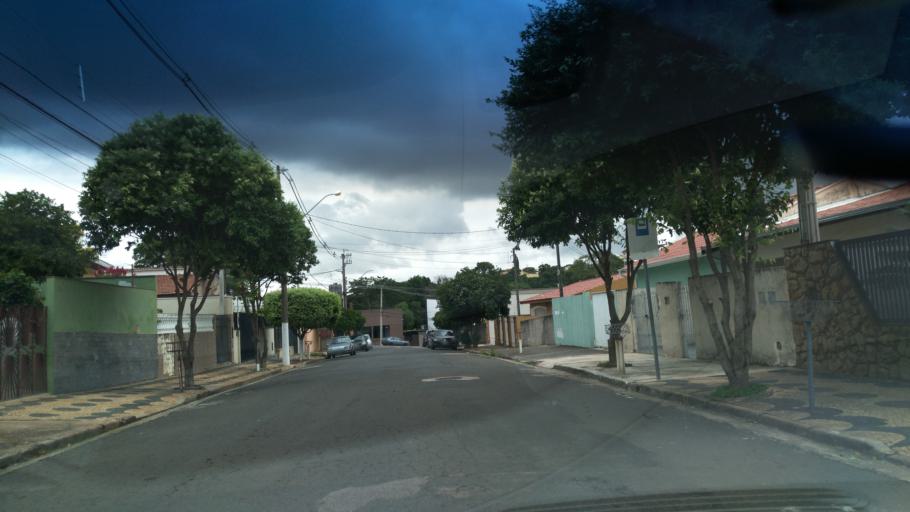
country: BR
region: Sao Paulo
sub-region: Valinhos
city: Valinhos
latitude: -22.9731
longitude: -46.9862
